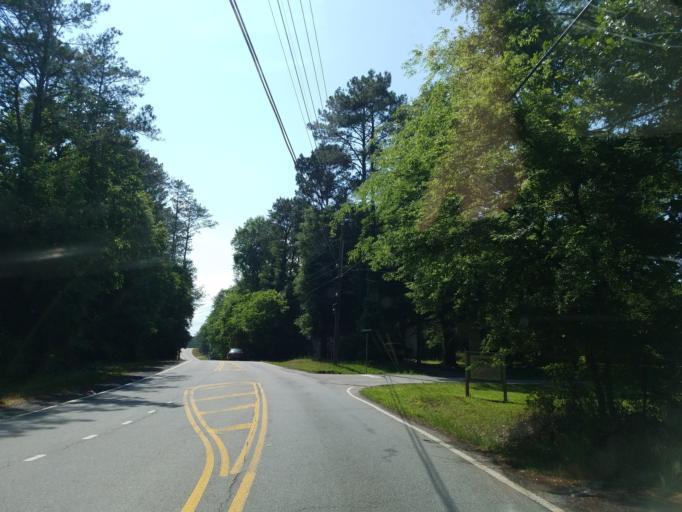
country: US
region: Georgia
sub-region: Cherokee County
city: Woodstock
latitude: 34.1189
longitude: -84.4830
